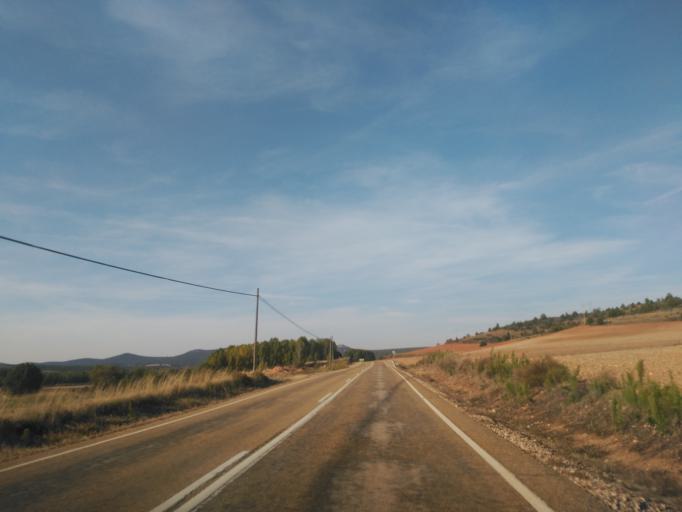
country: ES
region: Castille and Leon
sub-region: Provincia de Soria
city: Valdemaluque
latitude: 41.6806
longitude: -3.0445
